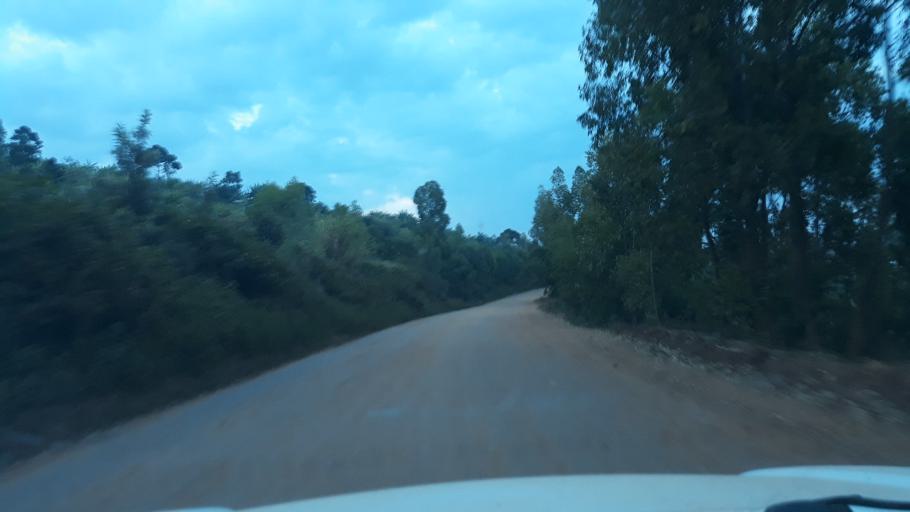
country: CD
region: South Kivu
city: Bukavu
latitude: -2.5727
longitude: 28.8548
